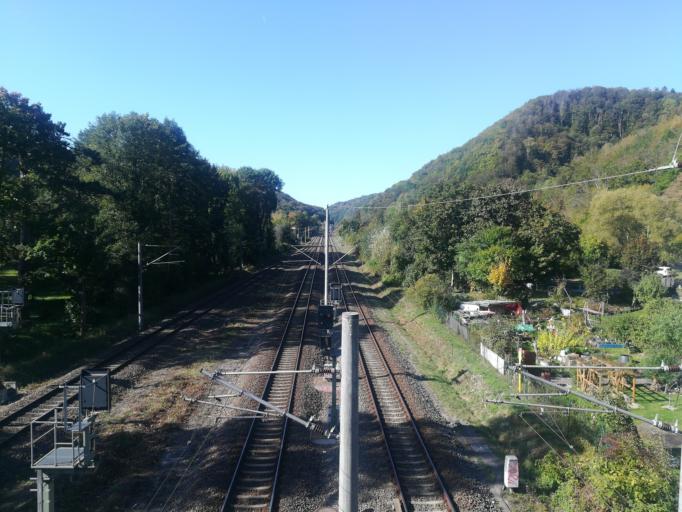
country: DE
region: Saxony
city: Rabenau
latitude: 50.9812
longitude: 13.6216
